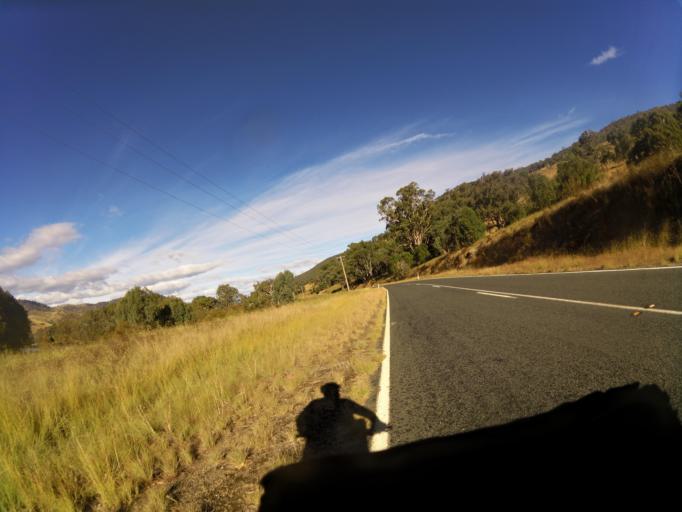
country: AU
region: New South Wales
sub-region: Greater Hume Shire
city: Holbrook
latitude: -35.9684
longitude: 147.7749
